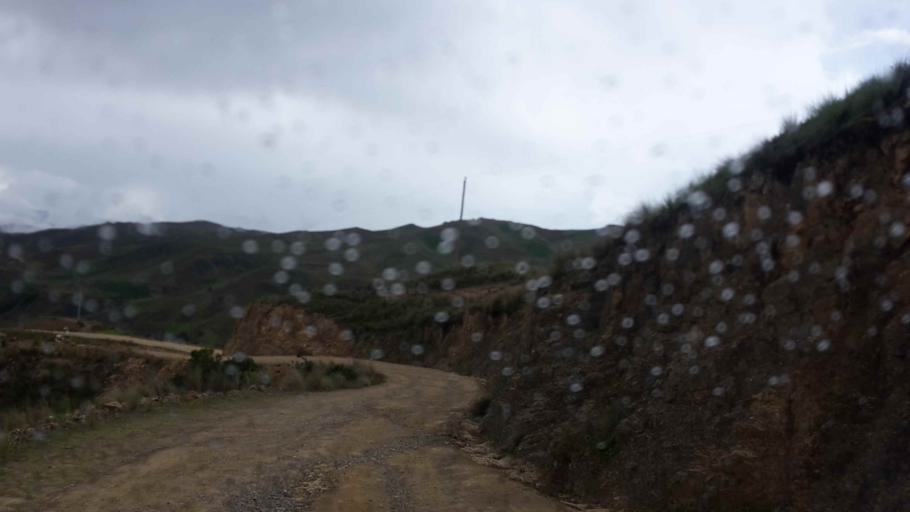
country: BO
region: Cochabamba
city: Cochabamba
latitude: -17.1424
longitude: -66.1038
